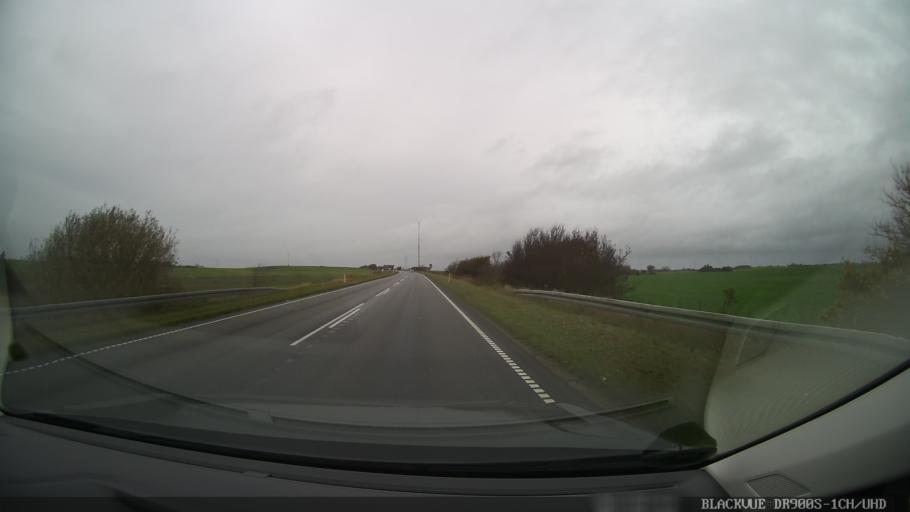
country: DK
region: North Denmark
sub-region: Morso Kommune
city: Nykobing Mors
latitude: 56.7921
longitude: 8.8135
